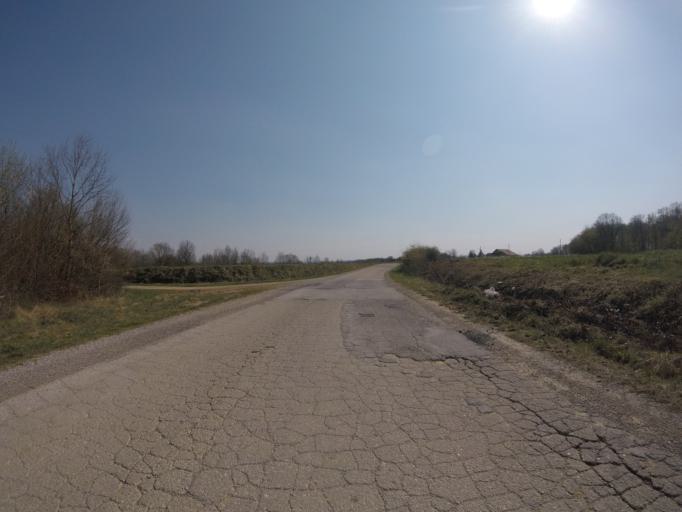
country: HR
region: Grad Zagreb
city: Strmec
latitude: 45.5572
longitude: 15.9030
